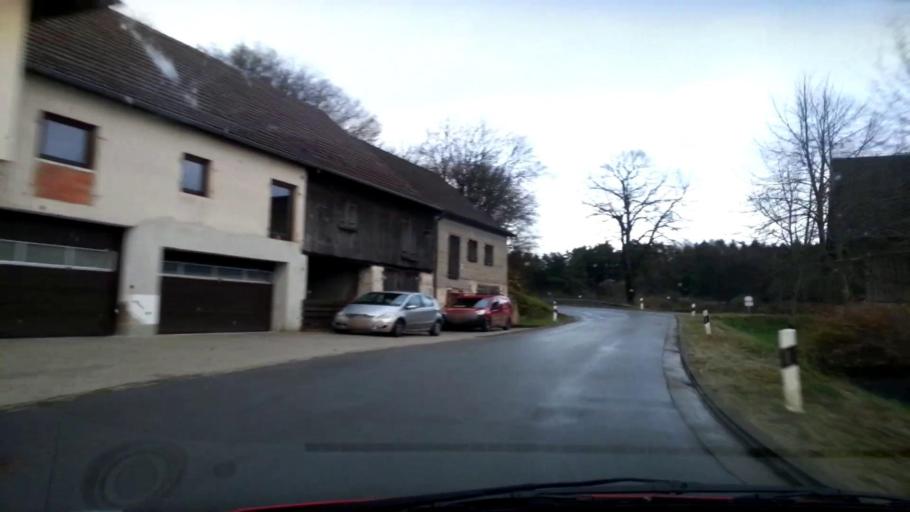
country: DE
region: Bavaria
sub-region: Upper Franconia
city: Aufsess
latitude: 49.9256
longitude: 11.2234
